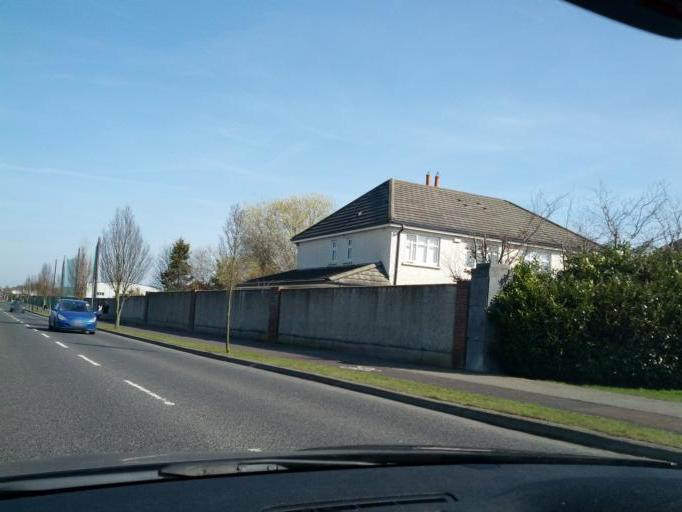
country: IE
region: Leinster
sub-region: Kildare
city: Celbridge
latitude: 53.3386
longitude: -6.5571
